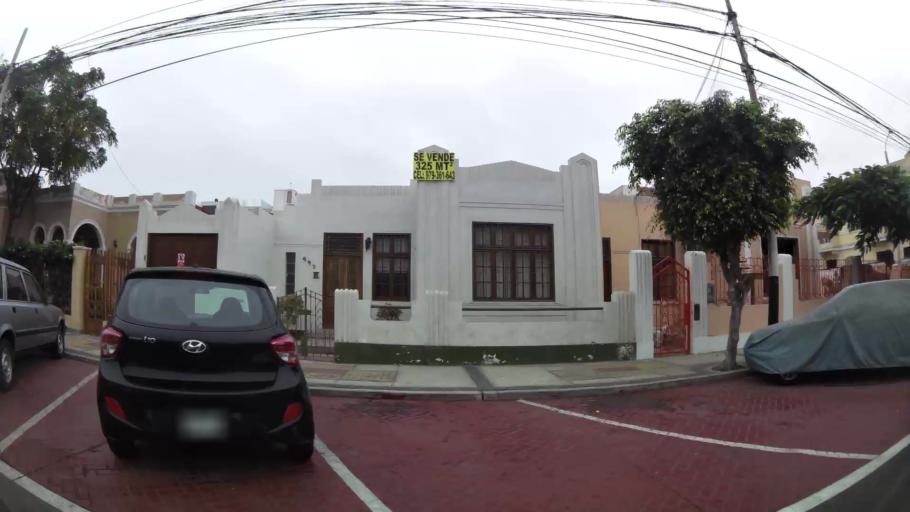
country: PE
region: Callao
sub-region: Callao
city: Callao
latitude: -12.0705
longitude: -77.1623
